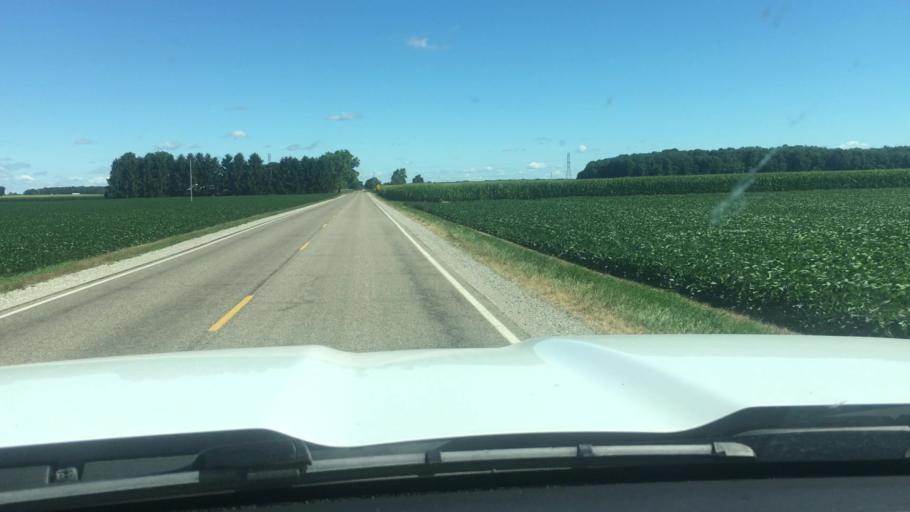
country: US
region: Michigan
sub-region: Montcalm County
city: Carson City
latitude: 43.2009
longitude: -84.7779
